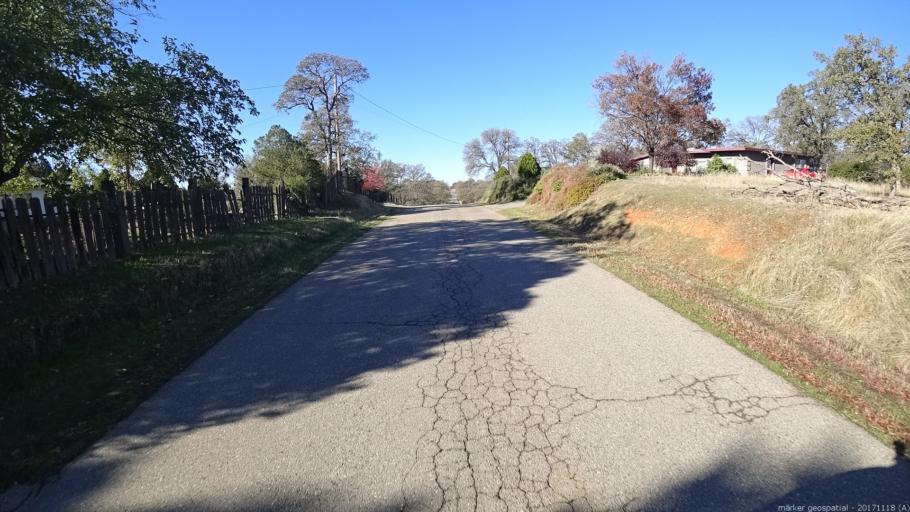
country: US
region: California
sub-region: Shasta County
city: Cottonwood
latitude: 40.3985
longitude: -122.3209
